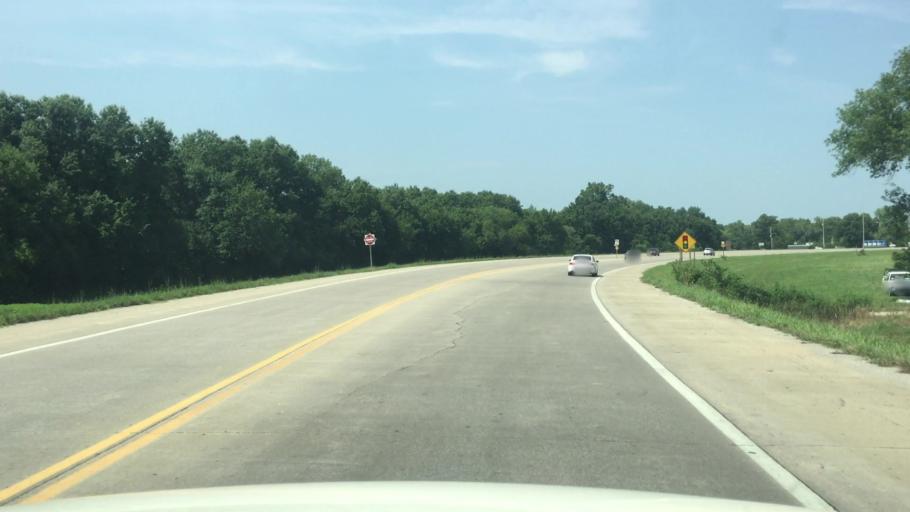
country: US
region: Kansas
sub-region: Crawford County
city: Pittsburg
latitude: 37.4069
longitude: -94.7245
